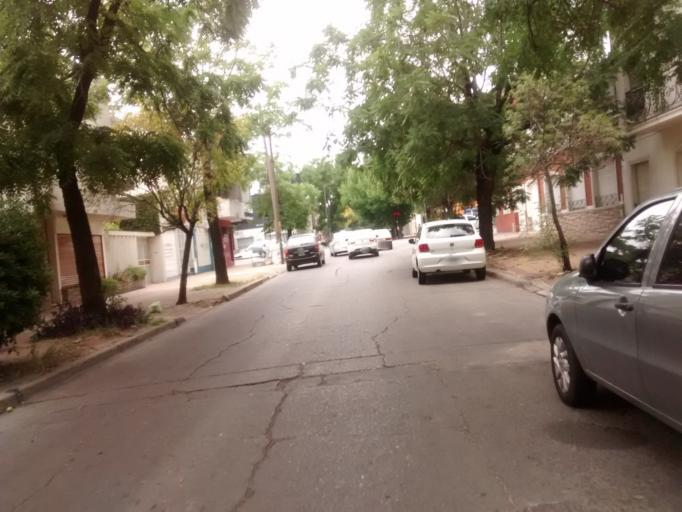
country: AR
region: Buenos Aires
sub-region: Partido de La Plata
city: La Plata
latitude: -34.9044
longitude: -57.9649
